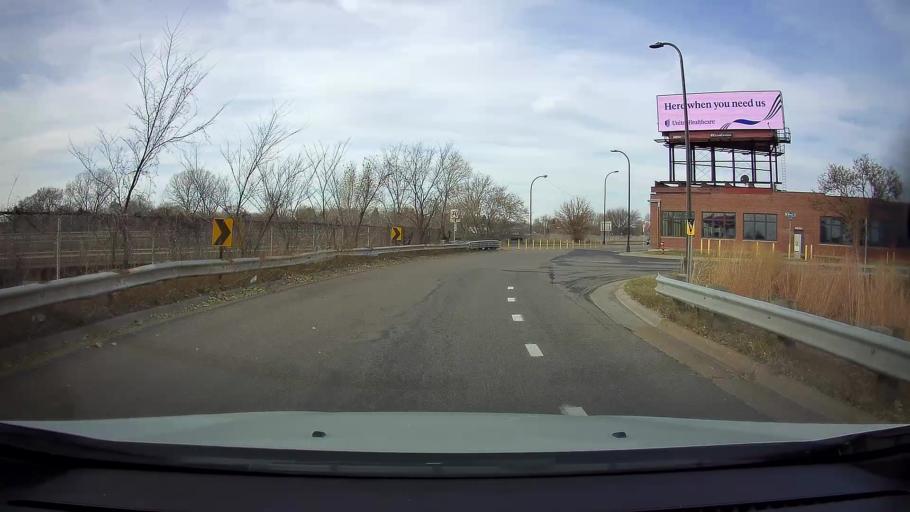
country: US
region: Minnesota
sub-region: Hennepin County
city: Minneapolis
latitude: 44.9929
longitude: -93.2368
